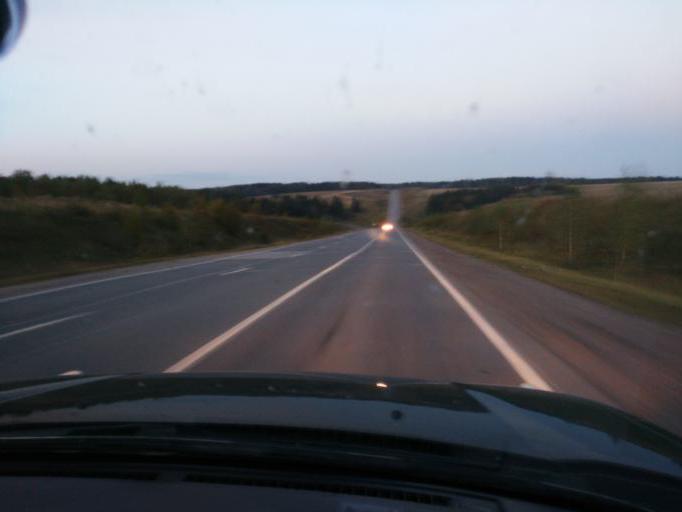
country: RU
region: Perm
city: Verkhnechusovskiye Gorodki
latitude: 58.2218
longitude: 57.1771
